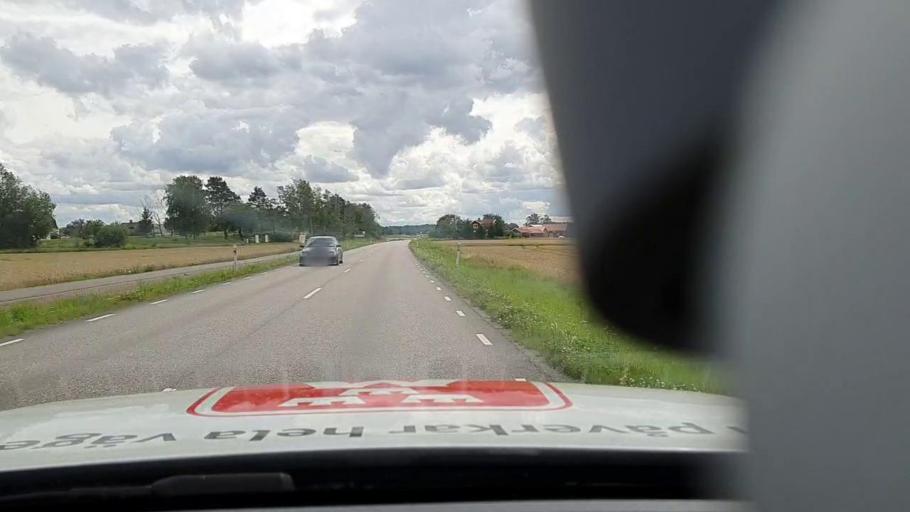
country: SE
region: Vaestra Goetaland
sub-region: Lidkopings Kommun
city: Lidkoping
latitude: 58.5496
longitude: 13.1149
